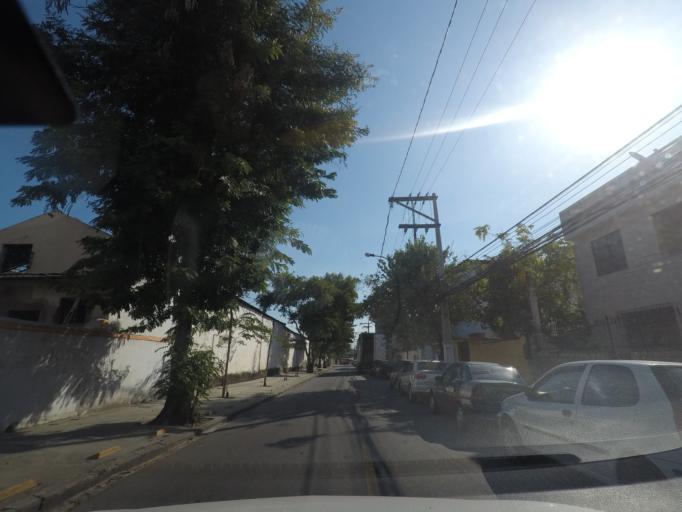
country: BR
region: Rio de Janeiro
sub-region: Niteroi
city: Niteroi
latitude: -22.8833
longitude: -43.1250
